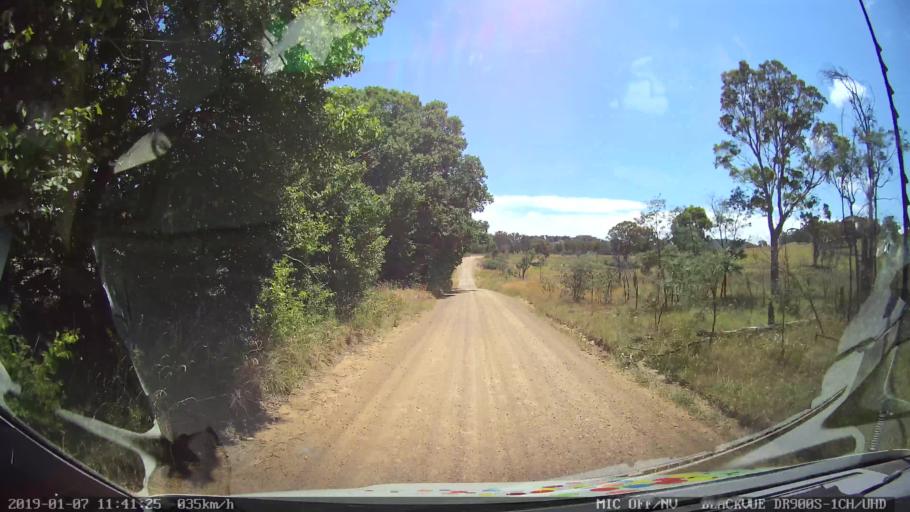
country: AU
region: New South Wales
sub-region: Guyra
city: Guyra
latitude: -30.3606
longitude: 151.5885
